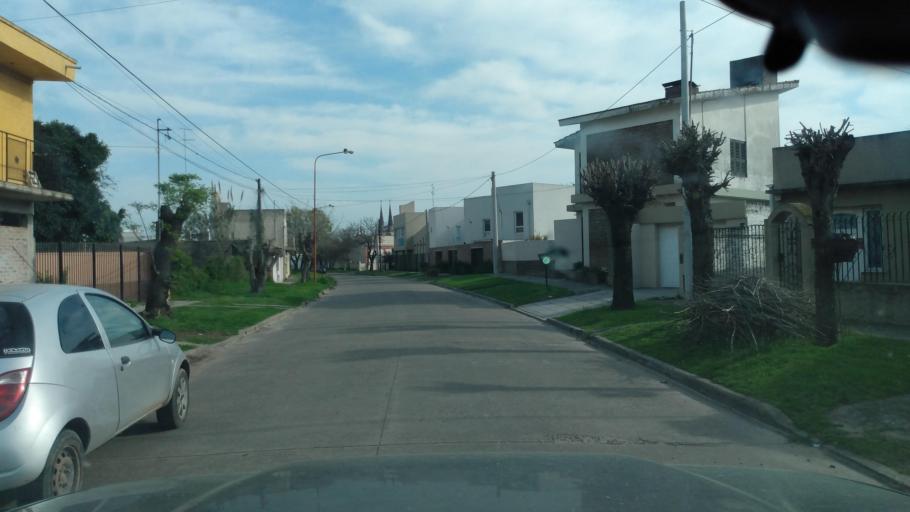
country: AR
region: Buenos Aires
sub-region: Partido de Lujan
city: Lujan
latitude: -34.5734
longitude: -59.1146
